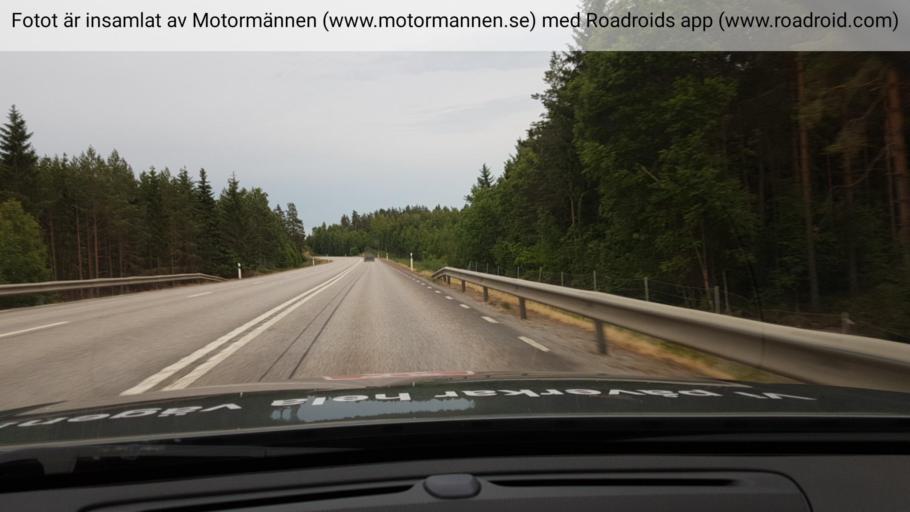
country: SE
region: OEstergoetland
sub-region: Motala Kommun
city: Borensberg
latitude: 58.5685
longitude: 15.3018
